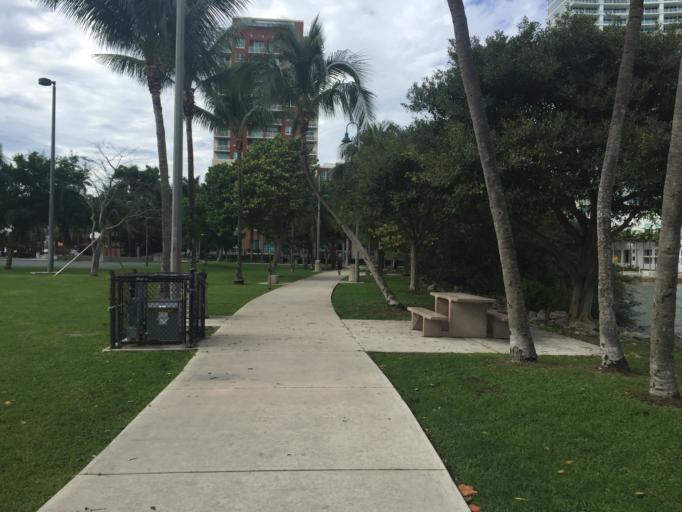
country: US
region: Florida
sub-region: Miami-Dade County
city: Miami
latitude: 25.7956
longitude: -80.1861
